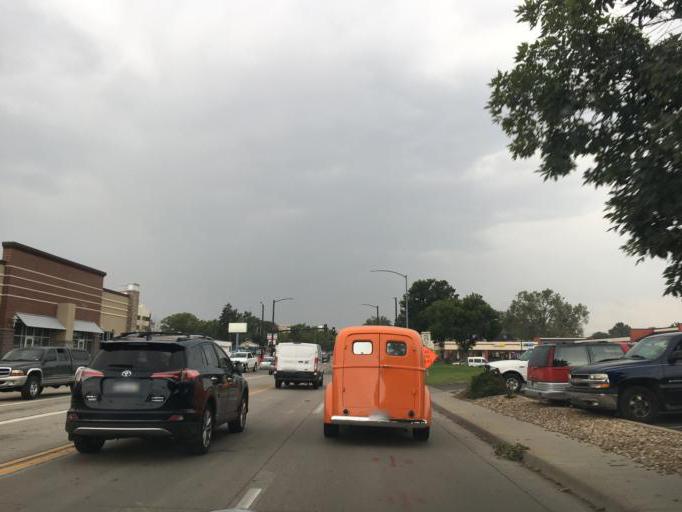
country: US
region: Colorado
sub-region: Jefferson County
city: Wheat Ridge
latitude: 39.7694
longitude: -105.0817
